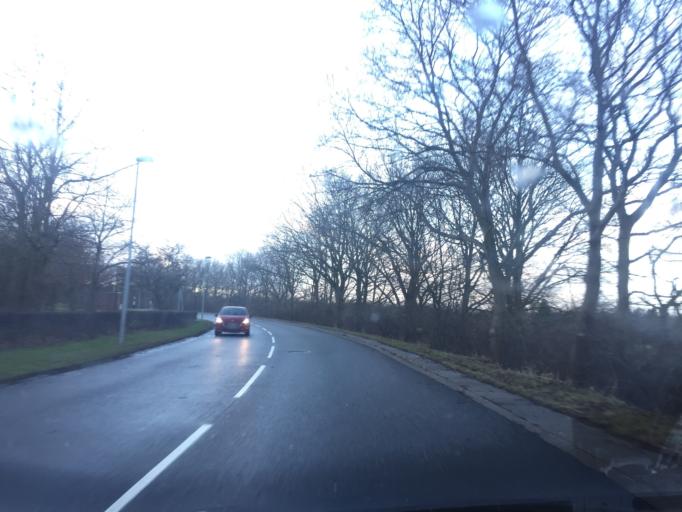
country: DK
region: Capital Region
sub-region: Hoje-Taastrup Kommune
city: Taastrup
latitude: 55.6601
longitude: 12.2700
